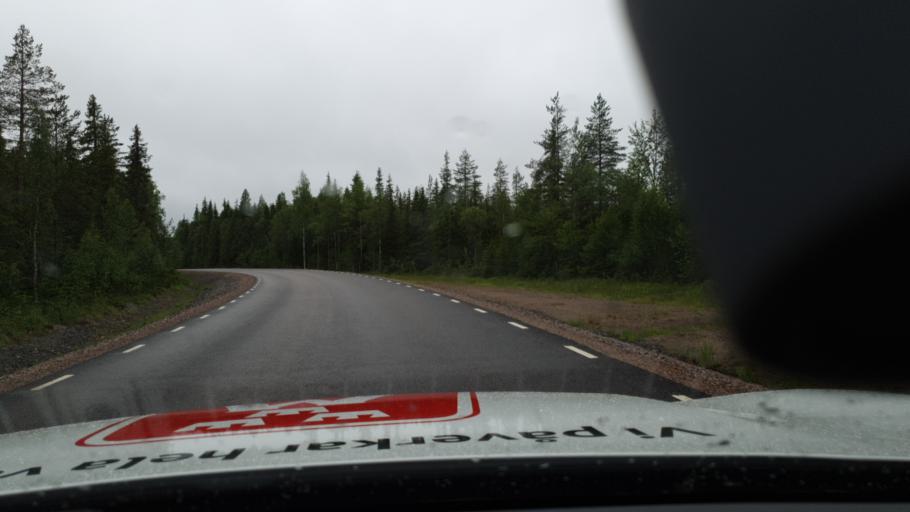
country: SE
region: Norrbotten
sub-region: Overtornea Kommun
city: OEvertornea
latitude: 66.5137
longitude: 23.3955
